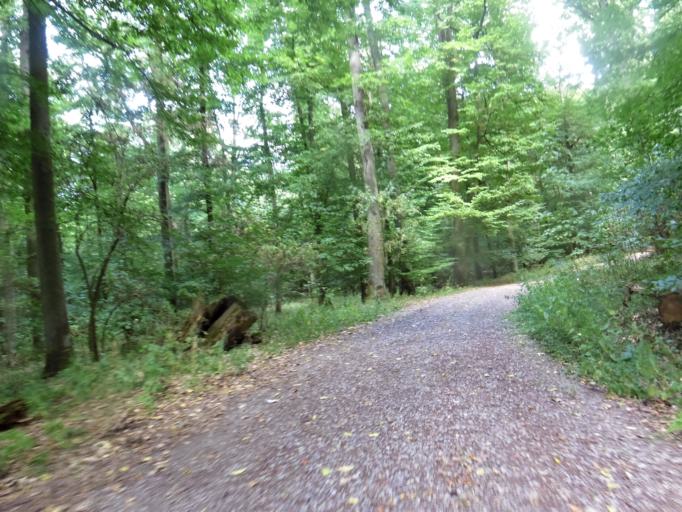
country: DE
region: Bavaria
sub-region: Regierungsbezirk Unterfranken
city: Waldbuttelbrunn
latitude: 49.7916
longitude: 9.8561
